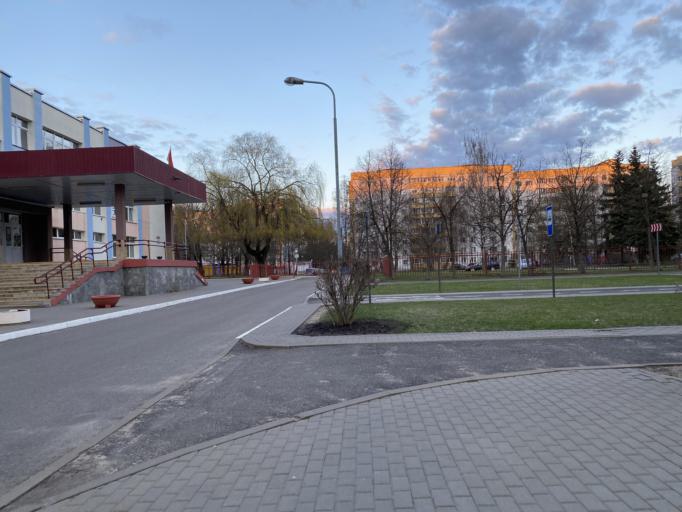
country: BY
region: Minsk
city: Bal'shavik
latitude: 53.9584
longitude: 27.6186
